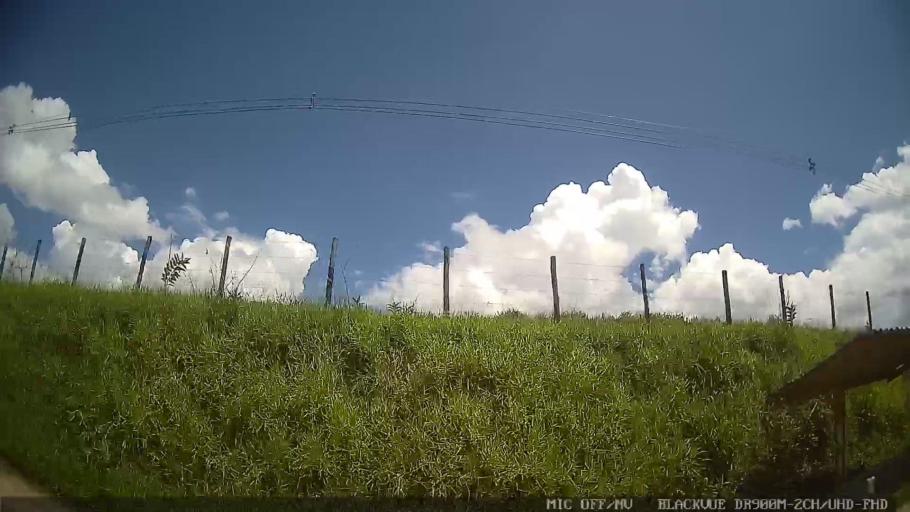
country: BR
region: Sao Paulo
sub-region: Caraguatatuba
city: Caraguatatuba
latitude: -23.5287
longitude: -45.5540
